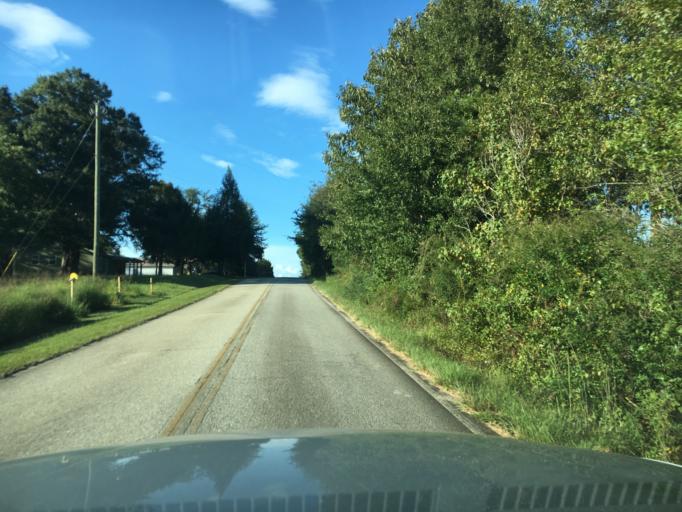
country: US
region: South Carolina
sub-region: Spartanburg County
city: Woodruff
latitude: 34.8020
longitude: -82.1031
